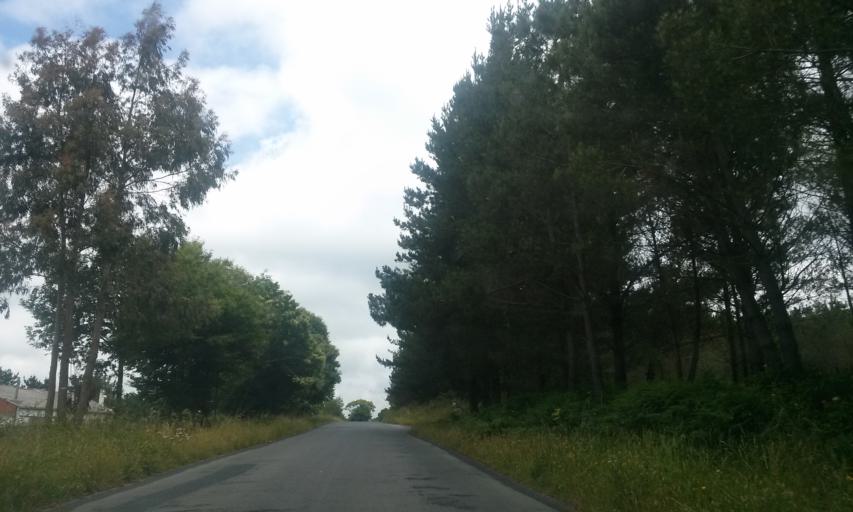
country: ES
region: Galicia
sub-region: Provincia de Lugo
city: Friol
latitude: 43.0811
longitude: -7.8157
